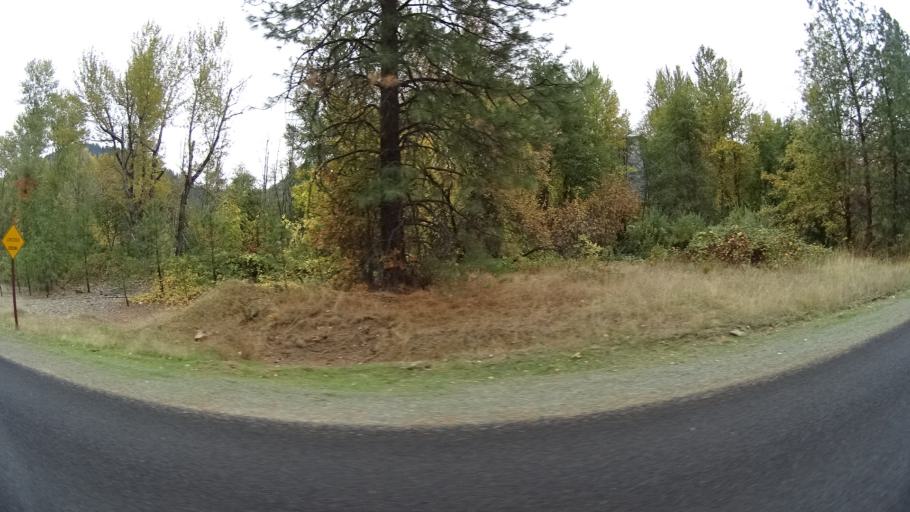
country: US
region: California
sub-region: Siskiyou County
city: Happy Camp
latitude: 41.8442
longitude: -123.1956
